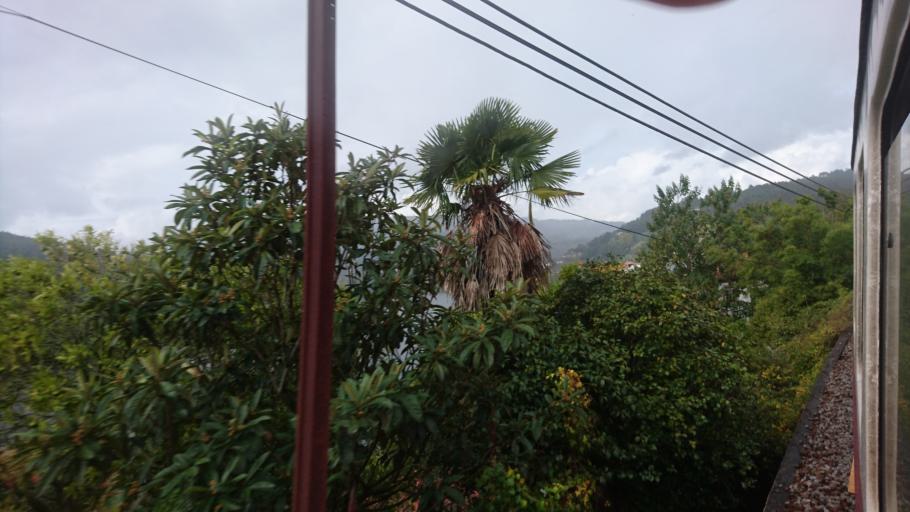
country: PT
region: Viseu
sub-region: Cinfaes
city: Cinfaes
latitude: 41.0954
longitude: -8.0815
